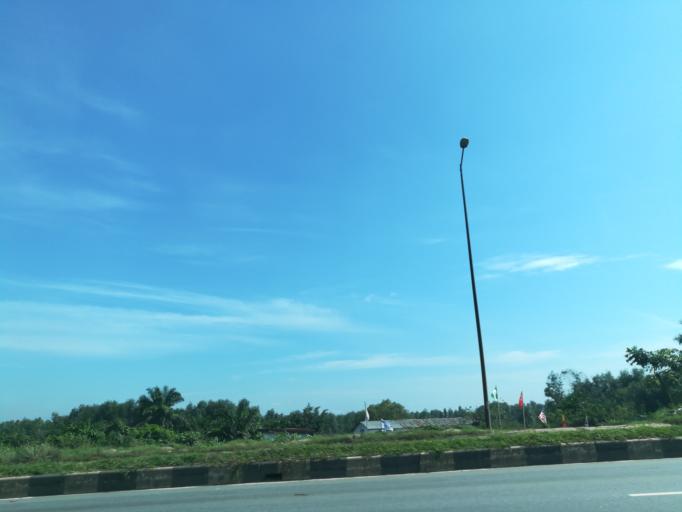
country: NG
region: Lagos
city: Ebute Ikorodu
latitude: 6.6206
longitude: 3.4566
